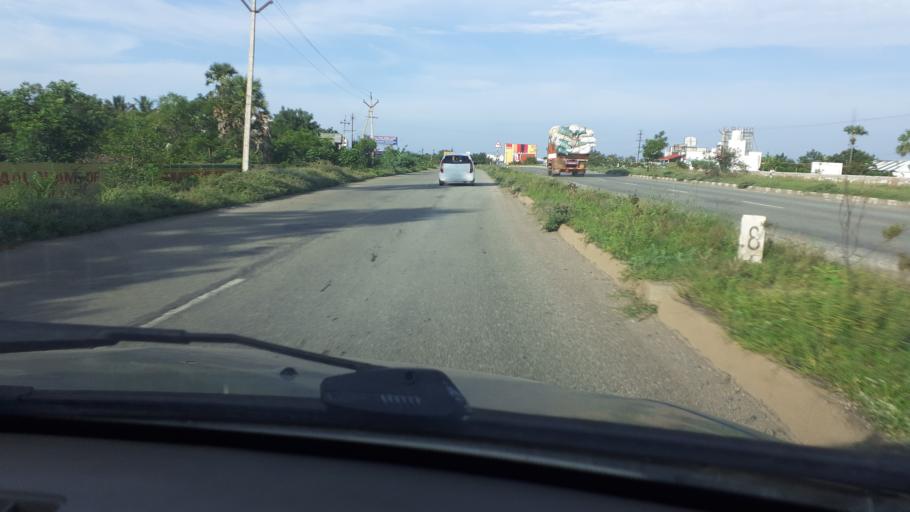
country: IN
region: Tamil Nadu
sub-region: Tirunelveli Kattabo
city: Tirunelveli
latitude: 8.6531
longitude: 77.7119
